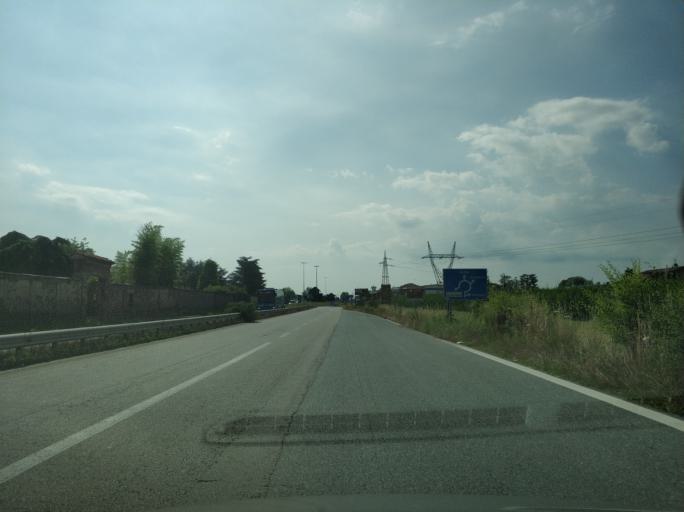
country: IT
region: Piedmont
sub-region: Provincia di Torino
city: Santena
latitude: 44.9578
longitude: 7.7854
